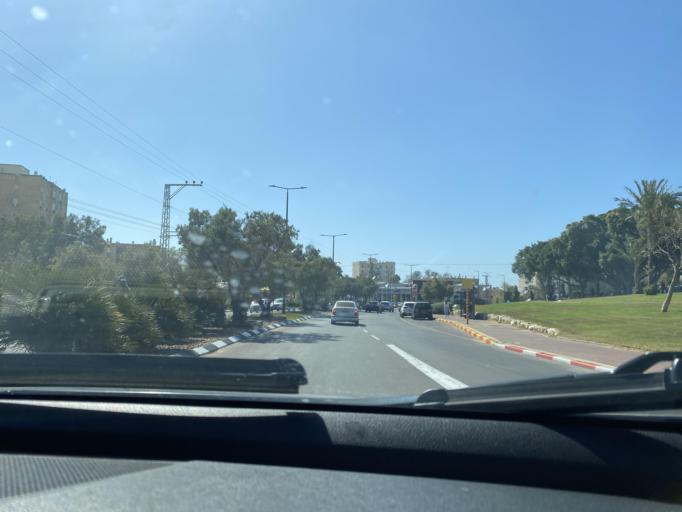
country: IL
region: Southern District
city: Ashqelon
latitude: 31.6804
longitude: 34.5723
